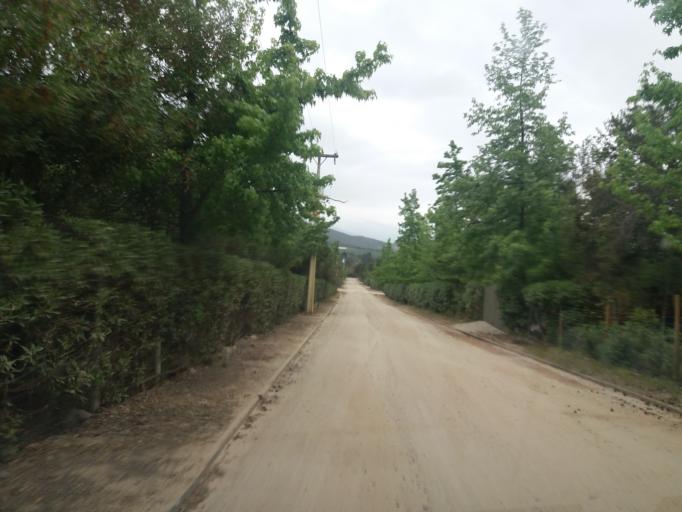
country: CL
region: Valparaiso
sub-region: Provincia de Marga Marga
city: Limache
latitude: -33.0258
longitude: -71.1359
